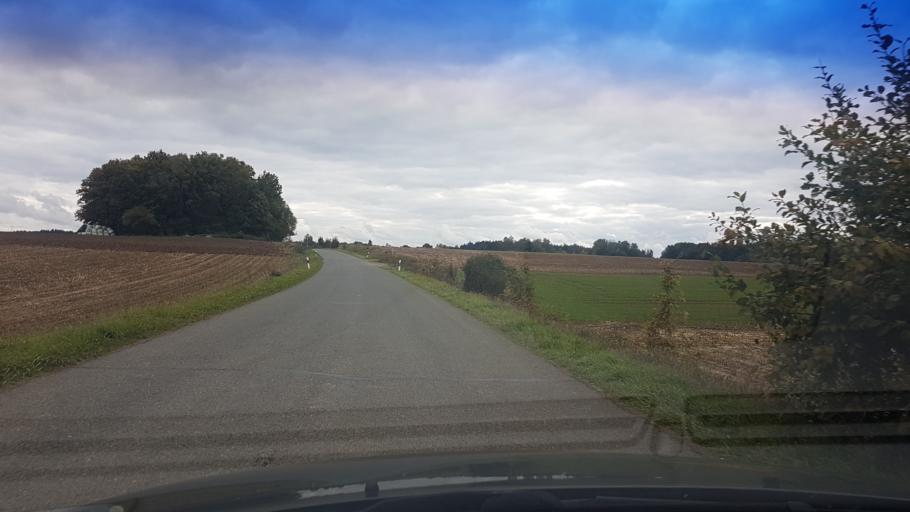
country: DE
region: Bavaria
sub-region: Upper Franconia
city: Wonsees
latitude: 50.0175
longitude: 11.2614
